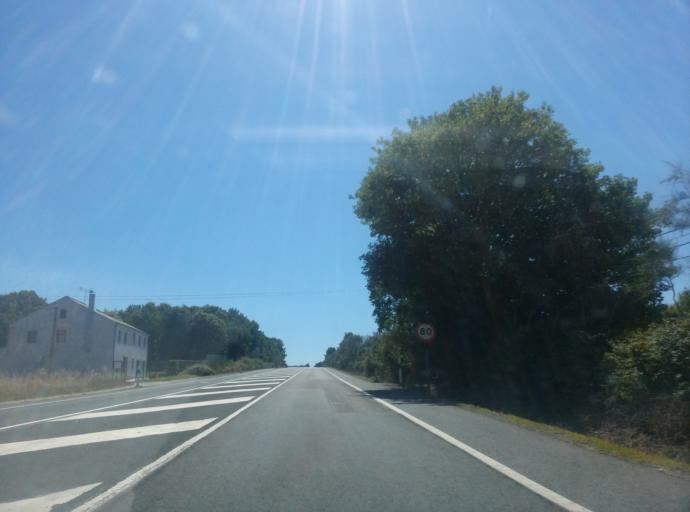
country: ES
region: Galicia
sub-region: Provincia de Lugo
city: Mos
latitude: 43.1087
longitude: -7.4581
